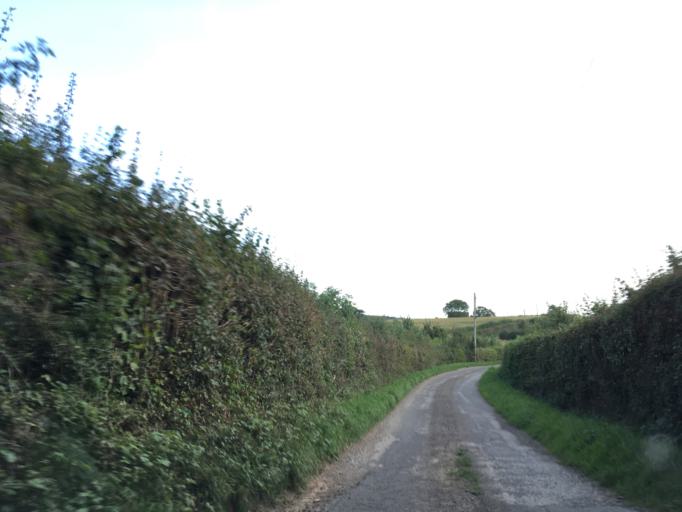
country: GB
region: England
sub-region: South Gloucestershire
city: Falfield
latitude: 51.6202
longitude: -2.4706
